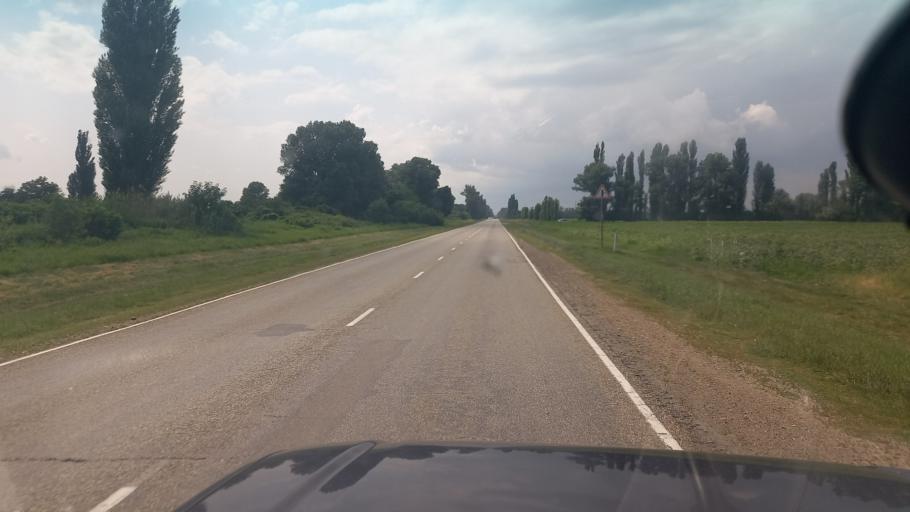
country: RU
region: Adygeya
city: Koshekhabl'
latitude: 44.9121
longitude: 40.4454
